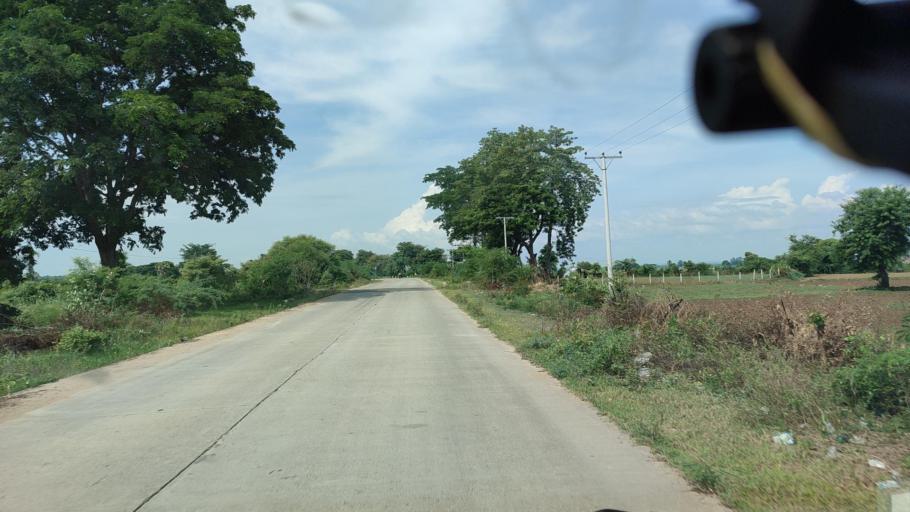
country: MM
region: Magway
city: Pakokku
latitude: 21.3302
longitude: 95.2516
